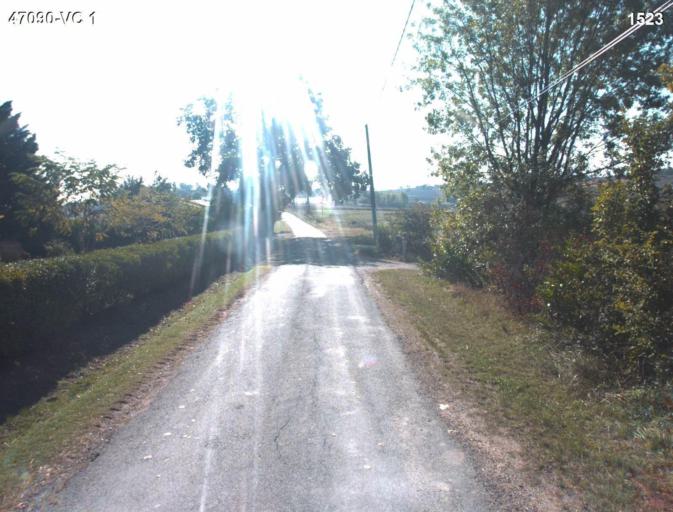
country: FR
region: Aquitaine
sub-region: Departement du Lot-et-Garonne
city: Nerac
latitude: 44.1621
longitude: 0.3854
